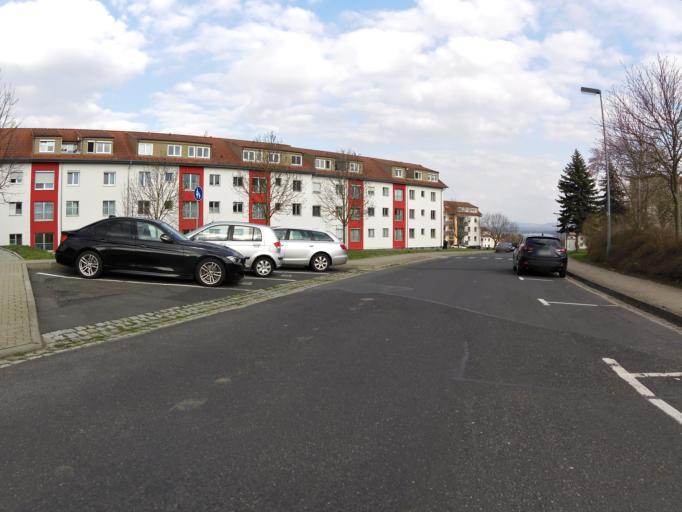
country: DE
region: Bavaria
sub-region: Regierungsbezirk Unterfranken
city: Kitzingen
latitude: 49.7394
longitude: 10.1331
